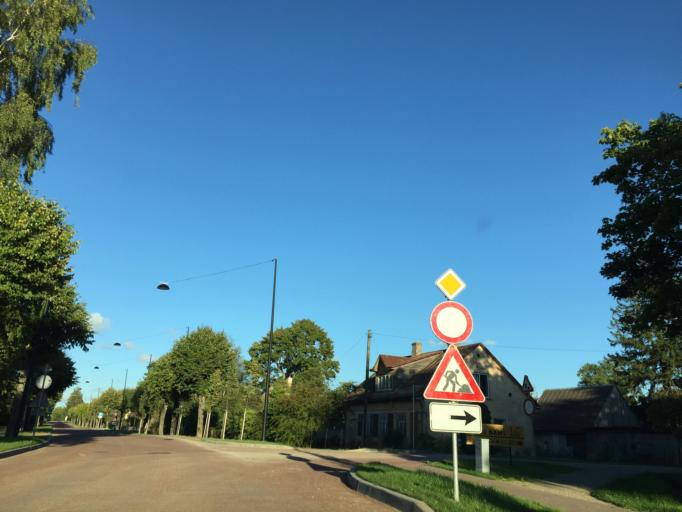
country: LV
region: Kuldigas Rajons
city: Kuldiga
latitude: 56.9711
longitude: 21.9903
